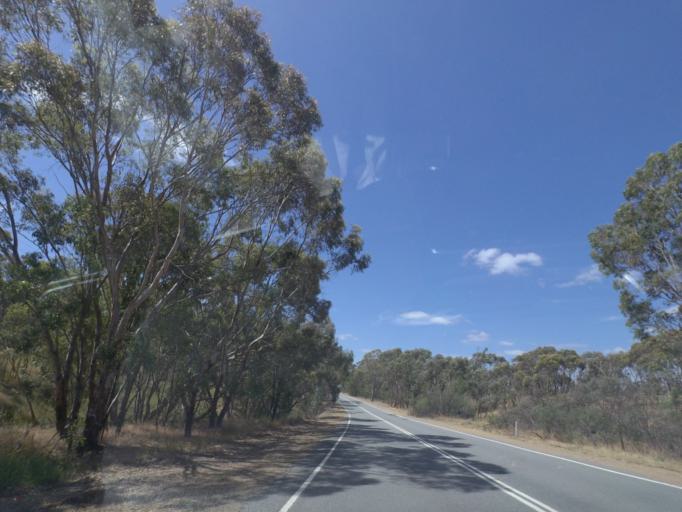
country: AU
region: Victoria
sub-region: Wangaratta
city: Wangaratta
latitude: -36.4598
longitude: 146.2343
